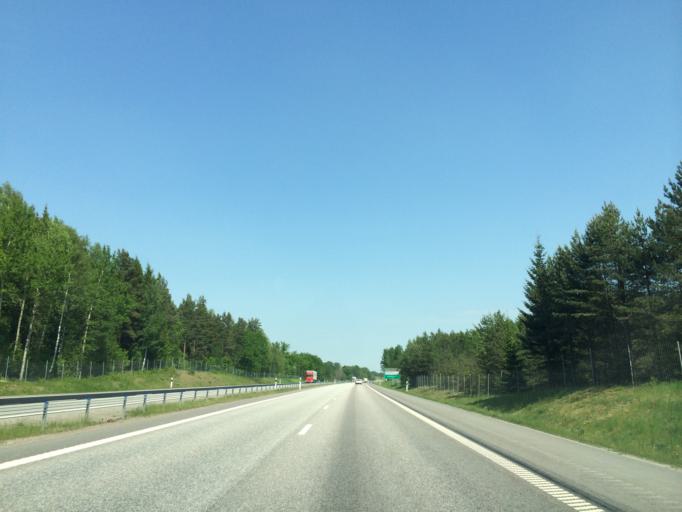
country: SE
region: OEstergoetland
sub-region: Linkopings Kommun
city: Malmslatt
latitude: 58.4228
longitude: 15.4907
